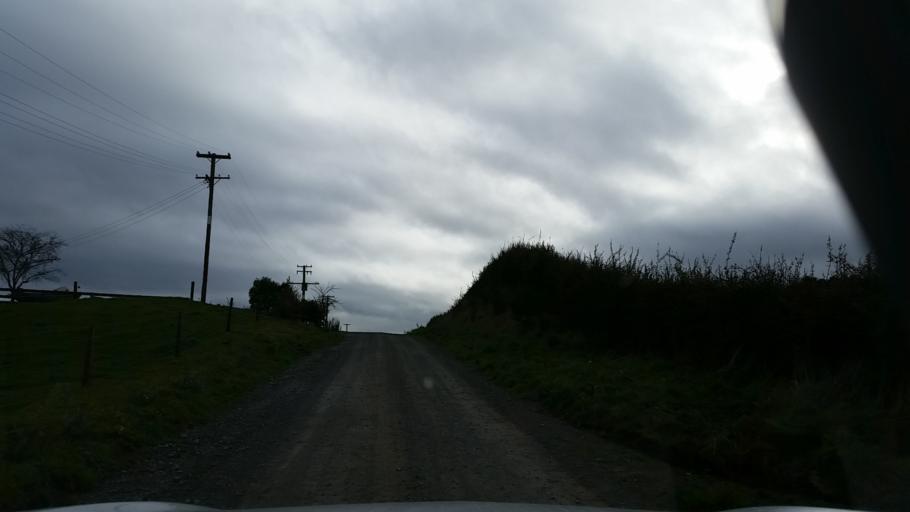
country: NZ
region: Bay of Plenty
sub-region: Whakatane District
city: Murupara
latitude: -38.3109
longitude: 176.4689
